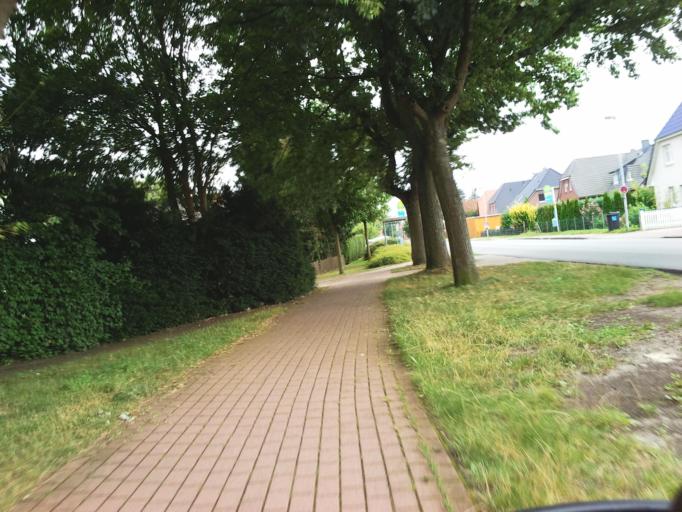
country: DE
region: Lower Saxony
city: Nienburg
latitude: 52.6701
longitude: 9.2380
